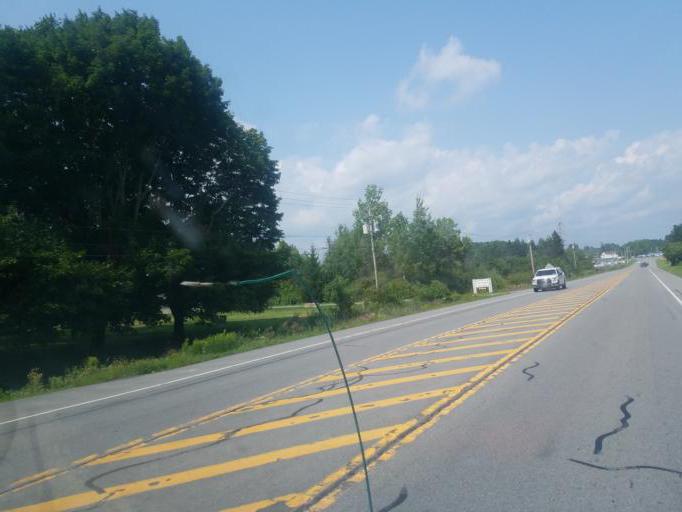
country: US
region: New York
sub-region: Fulton County
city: Johnstown
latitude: 42.9880
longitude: -74.3858
